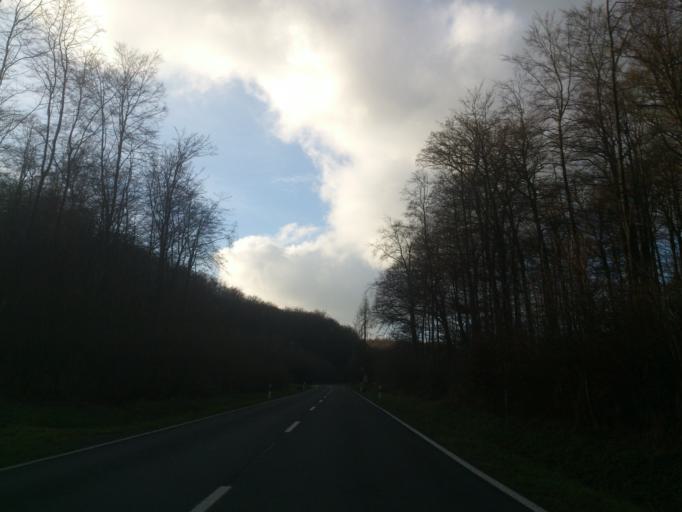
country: DE
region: North Rhine-Westphalia
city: Brakel
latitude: 51.7503
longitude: 9.2749
